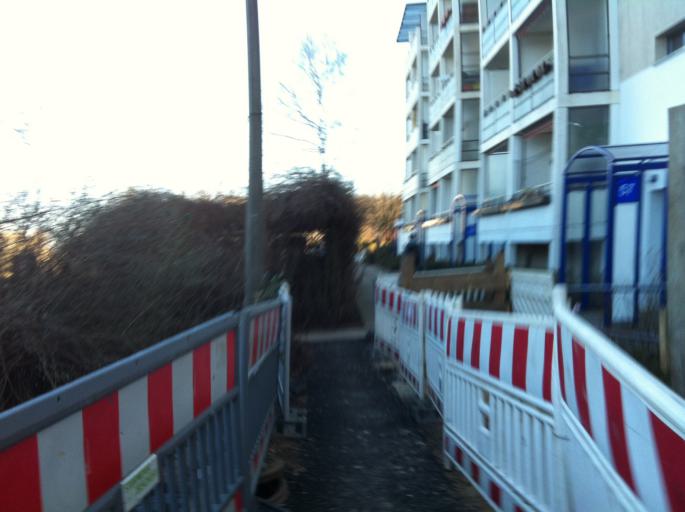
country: DE
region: Berlin
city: Kaulsdorf
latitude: 52.5264
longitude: 13.5831
